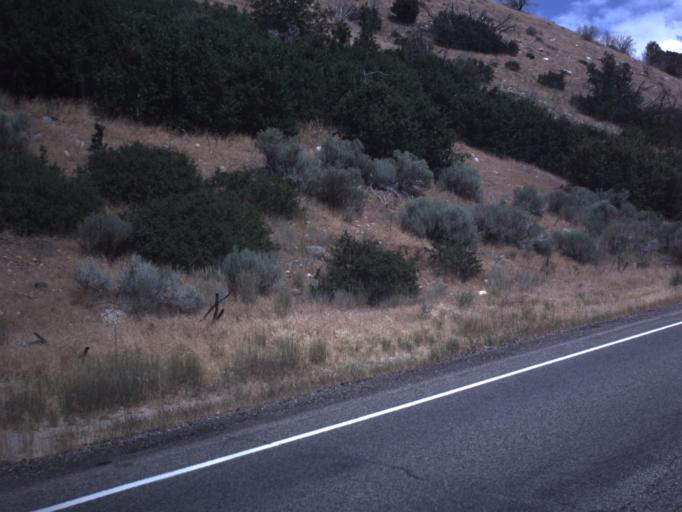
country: US
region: Utah
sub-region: Sanpete County
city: Fountain Green
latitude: 39.7053
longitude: -111.7097
